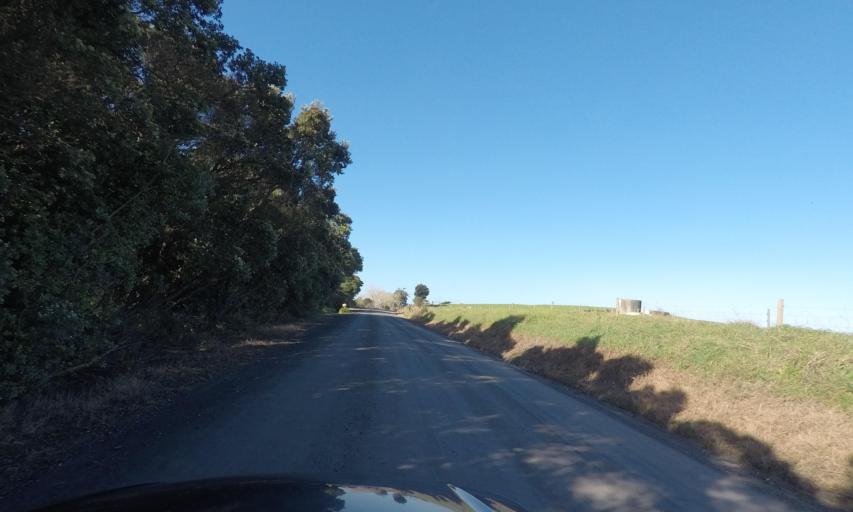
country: NZ
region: Auckland
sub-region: Auckland
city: Wellsford
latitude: -36.1542
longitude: 174.6014
